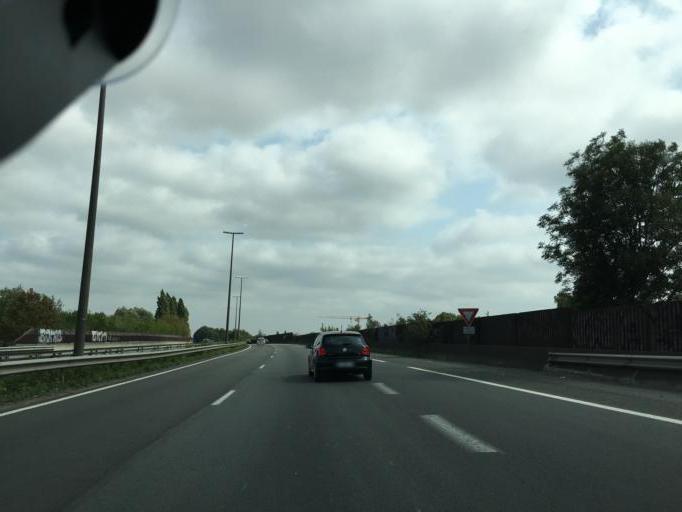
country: FR
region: Nord-Pas-de-Calais
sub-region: Departement du Pas-de-Calais
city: Montigny-en-Gohelle
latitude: 50.4318
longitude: 2.9293
